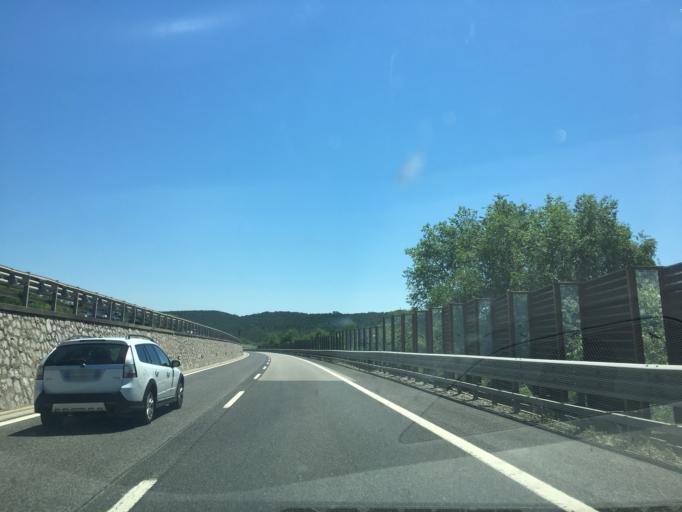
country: IT
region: Friuli Venezia Giulia
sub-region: Provincia di Gorizia
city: Ronchi dei Legionari
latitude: 45.8226
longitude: 13.5276
